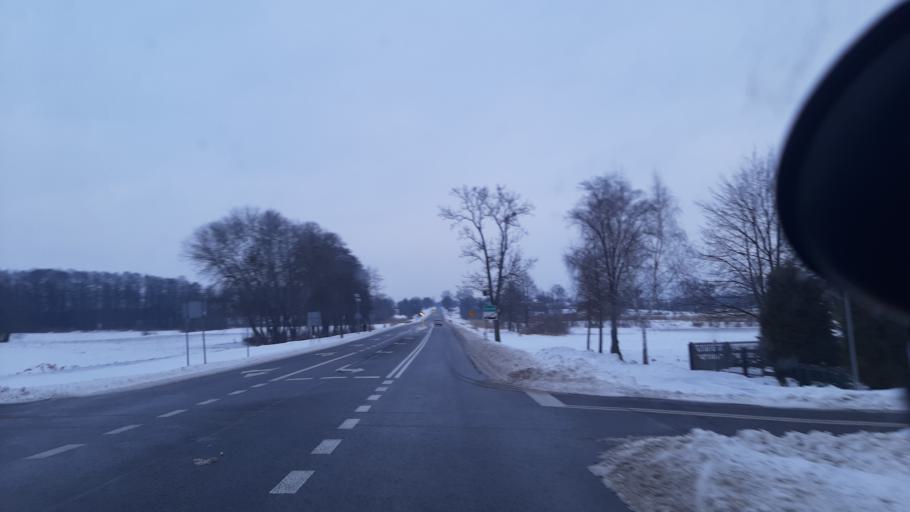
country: PL
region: Lublin Voivodeship
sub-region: Powiat lubelski
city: Garbow
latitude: 51.3622
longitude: 22.3051
